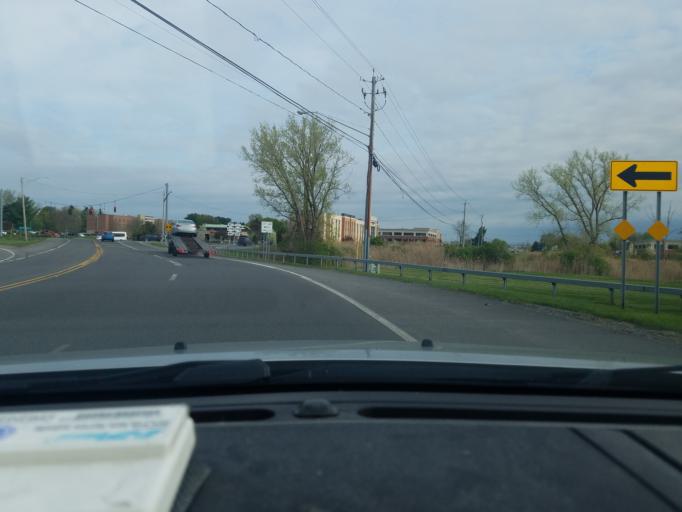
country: US
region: New York
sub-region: Onondaga County
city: East Syracuse
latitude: 43.0870
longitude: -76.0782
